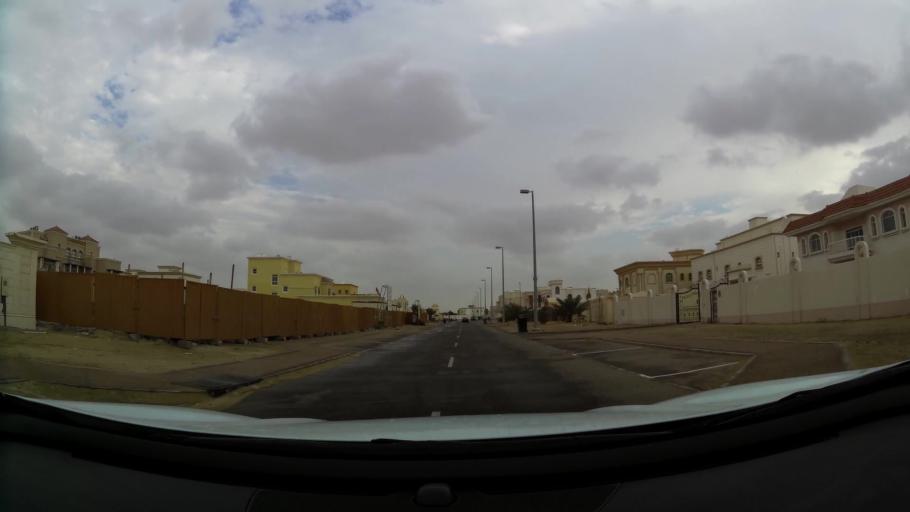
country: AE
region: Abu Dhabi
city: Abu Dhabi
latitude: 24.3530
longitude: 54.6285
